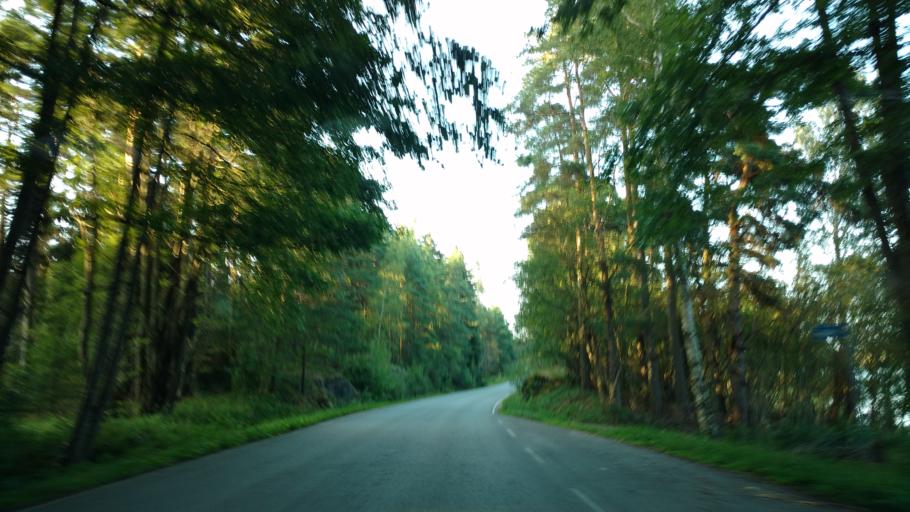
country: FI
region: Varsinais-Suomi
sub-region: Aboland-Turunmaa
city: Dragsfjaerd
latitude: 59.9786
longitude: 22.4497
